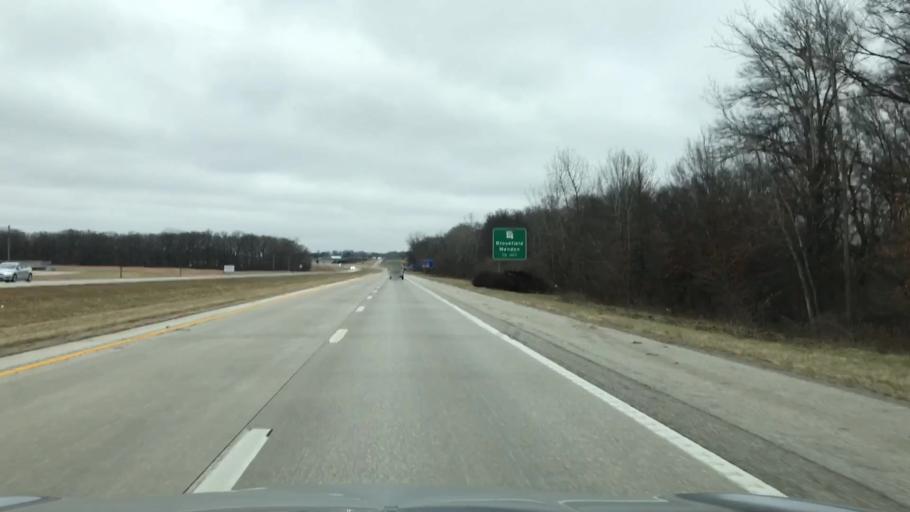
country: US
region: Missouri
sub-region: Linn County
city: Brookfield
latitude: 39.7754
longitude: -93.0891
